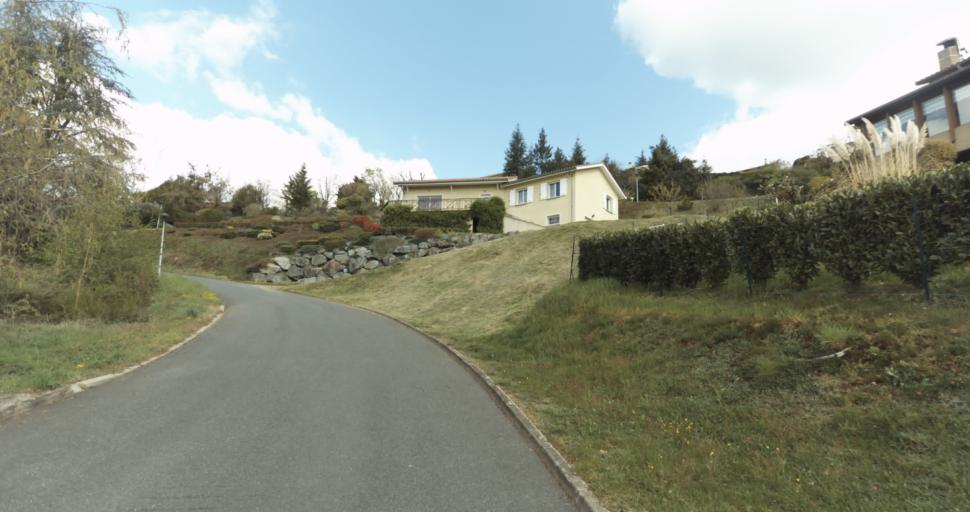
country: FR
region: Rhone-Alpes
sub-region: Departement du Rhone
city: Tarare
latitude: 45.8986
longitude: 4.4440
